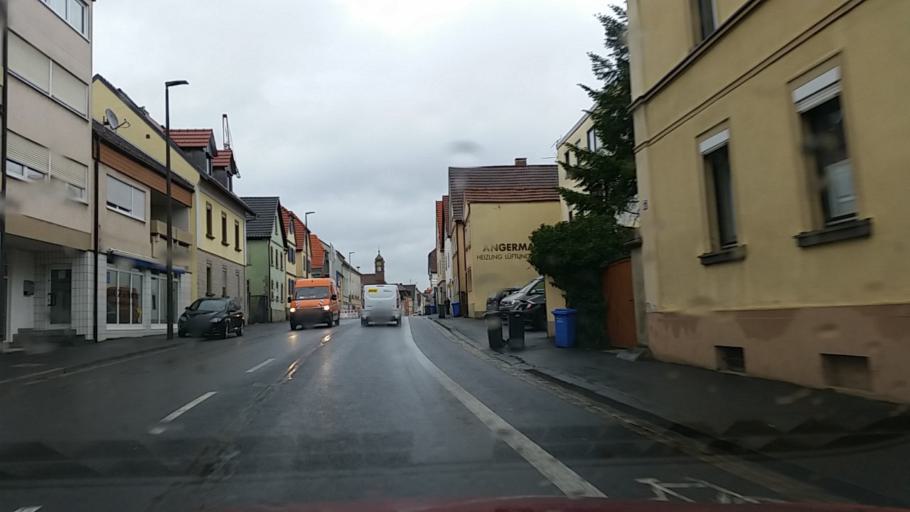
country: DE
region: Bavaria
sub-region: Regierungsbezirk Unterfranken
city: Bergrheinfeld
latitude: 50.0267
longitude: 10.2000
